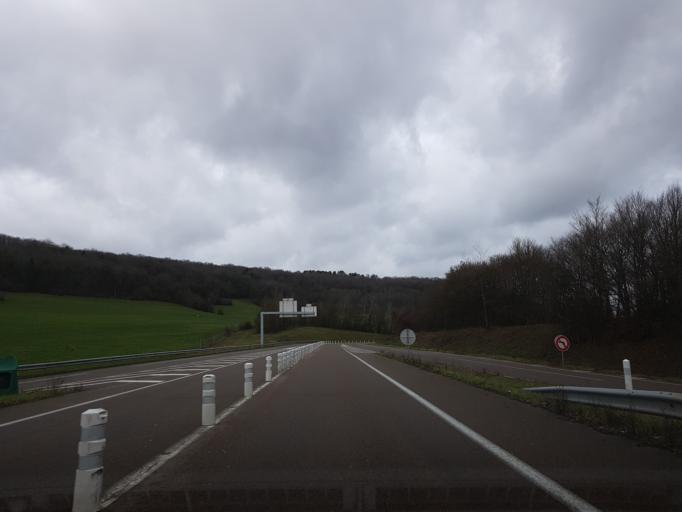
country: FR
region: Champagne-Ardenne
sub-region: Departement de la Haute-Marne
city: Rolampont
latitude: 47.9313
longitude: 5.2868
